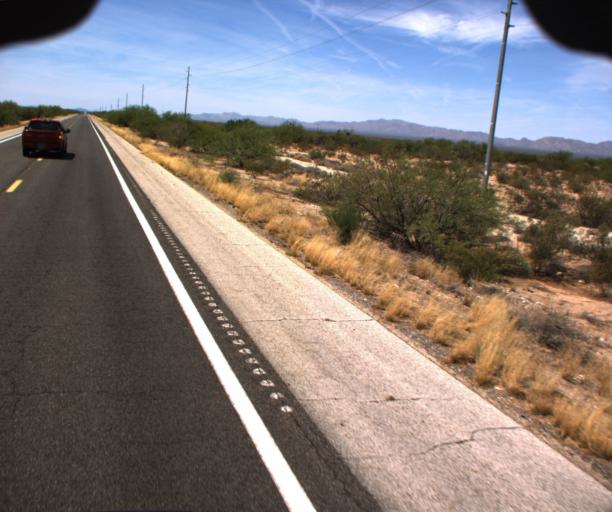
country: US
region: Arizona
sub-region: La Paz County
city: Salome
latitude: 33.8931
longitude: -113.3272
